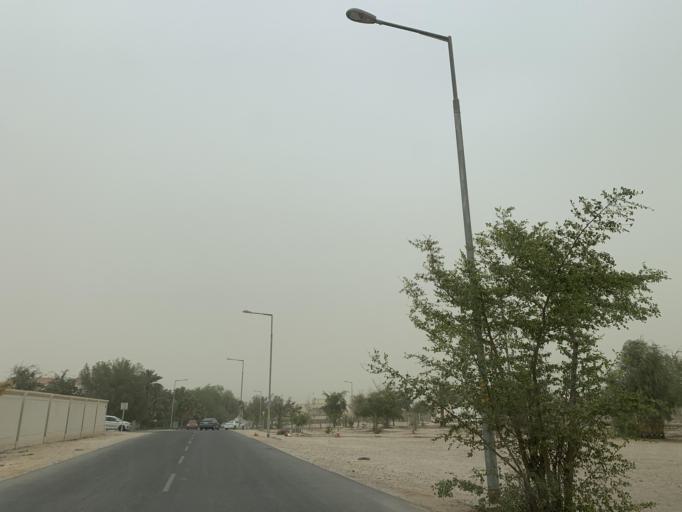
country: BH
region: Northern
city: Ar Rifa'
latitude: 26.1358
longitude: 50.5373
